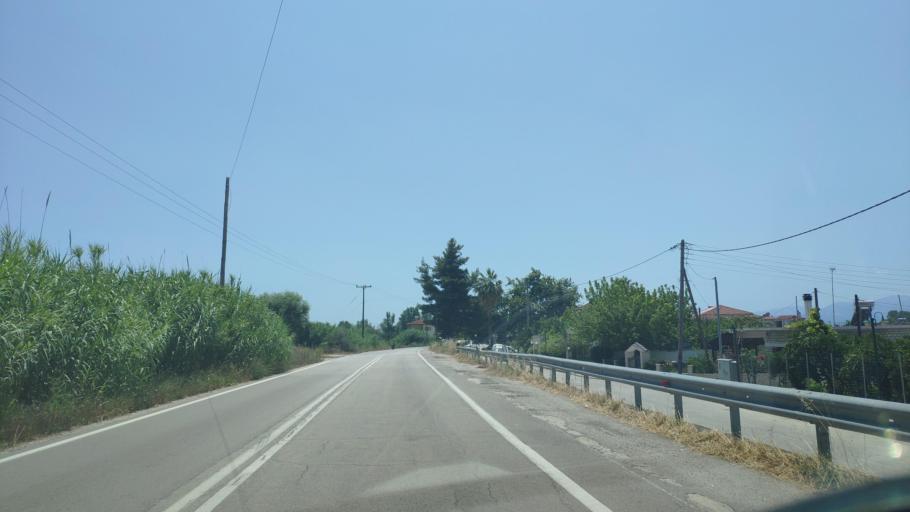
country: GR
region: Epirus
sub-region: Nomos Artas
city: Neochori
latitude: 39.0848
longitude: 21.0169
